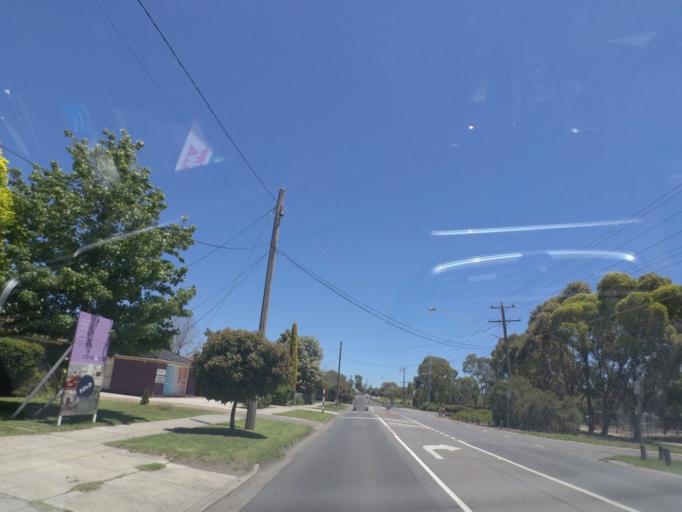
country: AU
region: Victoria
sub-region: Whittlesea
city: Epping
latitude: -37.6452
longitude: 145.0336
